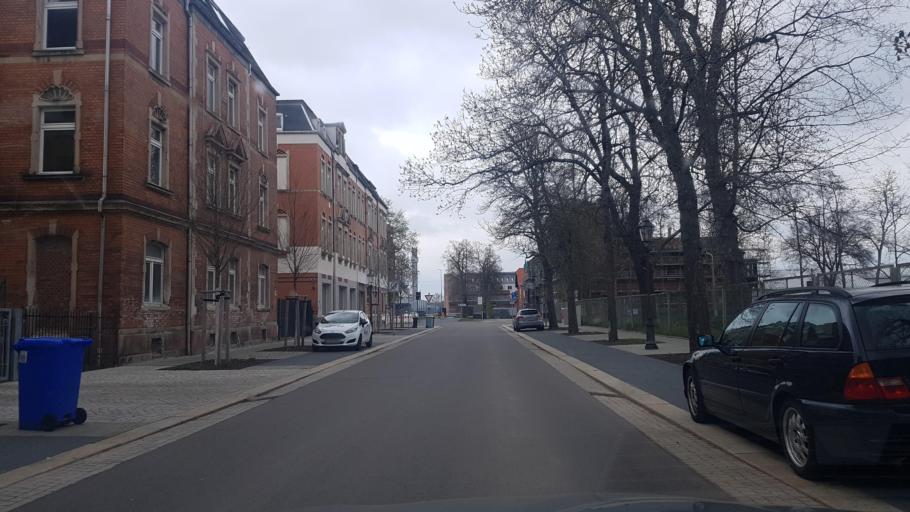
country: DE
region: Saxony
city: Zwickau
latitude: 50.7346
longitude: 12.4838
